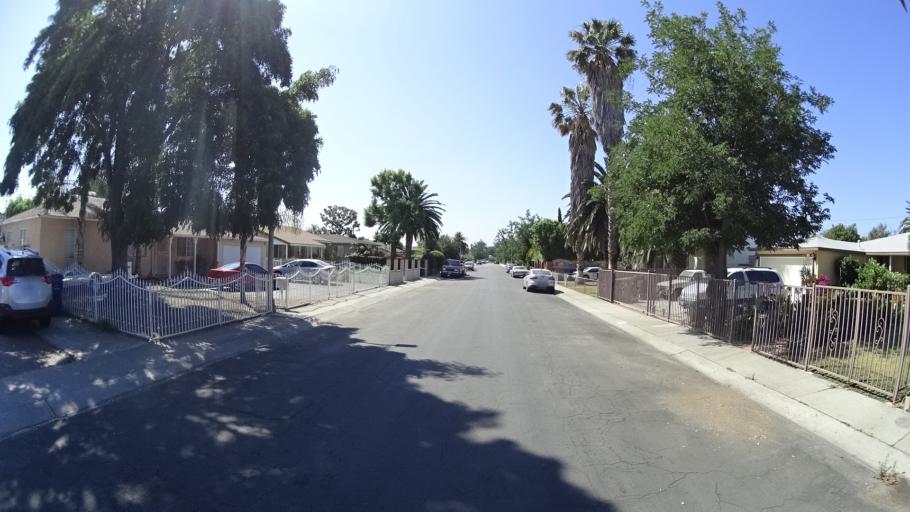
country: US
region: California
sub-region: Los Angeles County
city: Van Nuys
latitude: 34.2276
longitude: -118.4451
